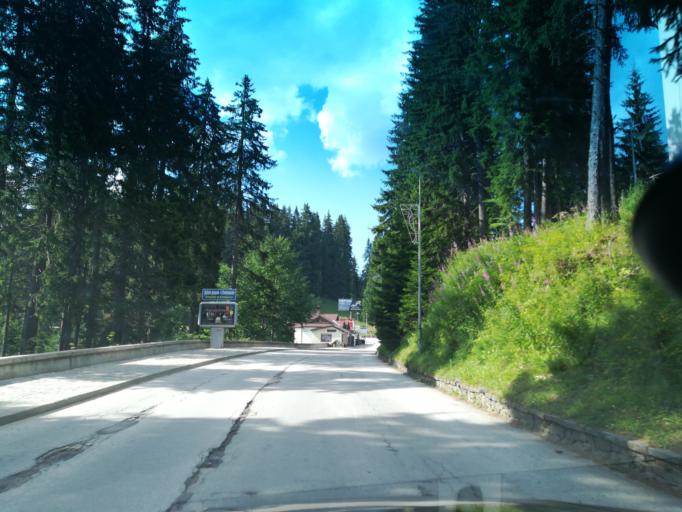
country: BG
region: Smolyan
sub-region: Obshtina Smolyan
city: Smolyan
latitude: 41.6525
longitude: 24.6940
